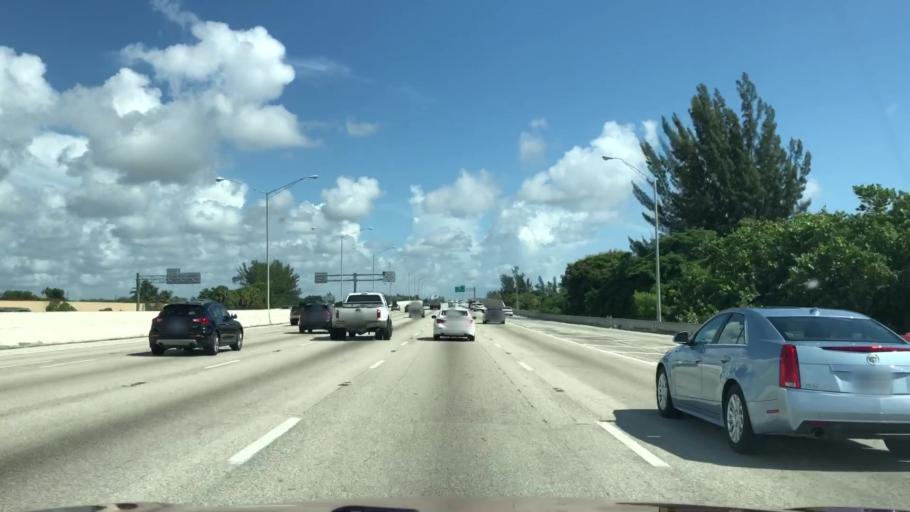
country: US
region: Florida
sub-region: Palm Beach County
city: Lake Clarke Shores
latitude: 26.6304
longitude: -80.0733
